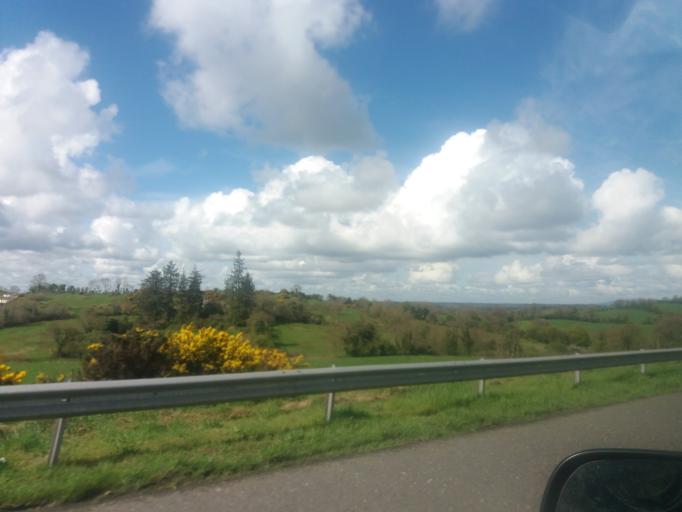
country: IE
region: Ulster
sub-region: An Cabhan
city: Cavan
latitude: 54.0216
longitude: -7.3497
